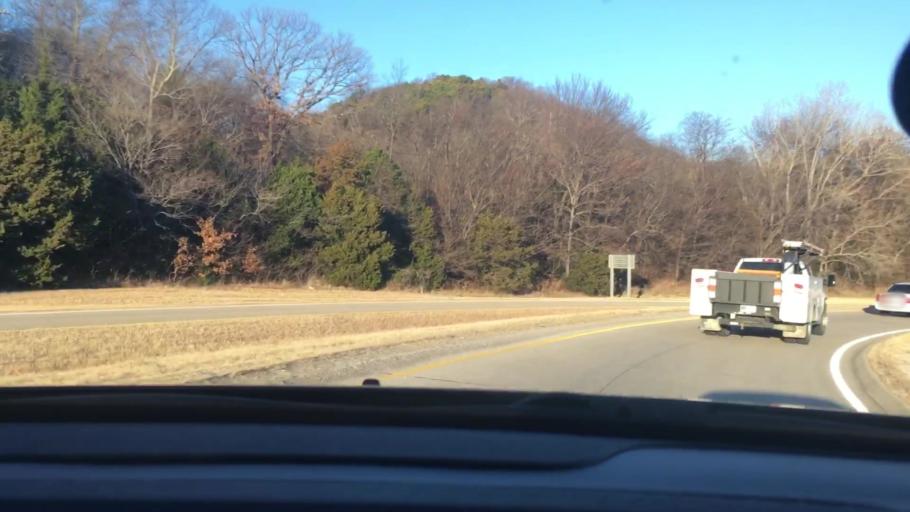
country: US
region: Oklahoma
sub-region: Murray County
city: Davis
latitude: 34.4495
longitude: -97.1365
